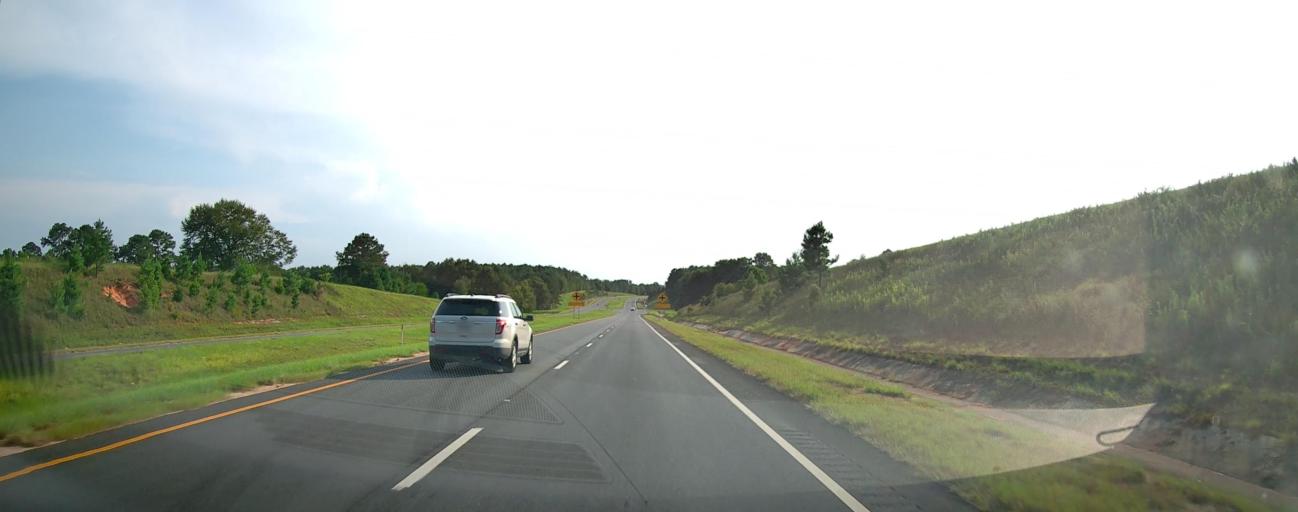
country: US
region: Georgia
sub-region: Taylor County
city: Butler
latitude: 32.5460
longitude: -84.2222
